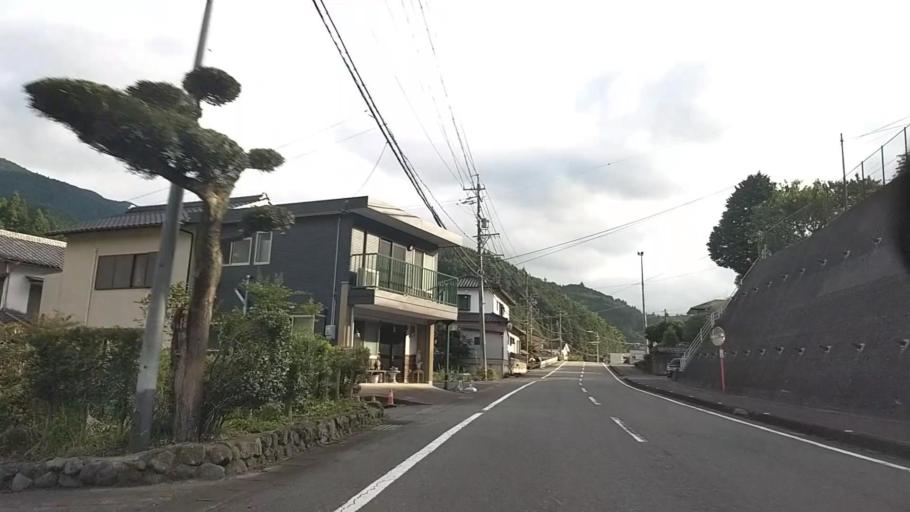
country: JP
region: Shizuoka
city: Fujinomiya
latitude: 35.1833
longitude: 138.5459
